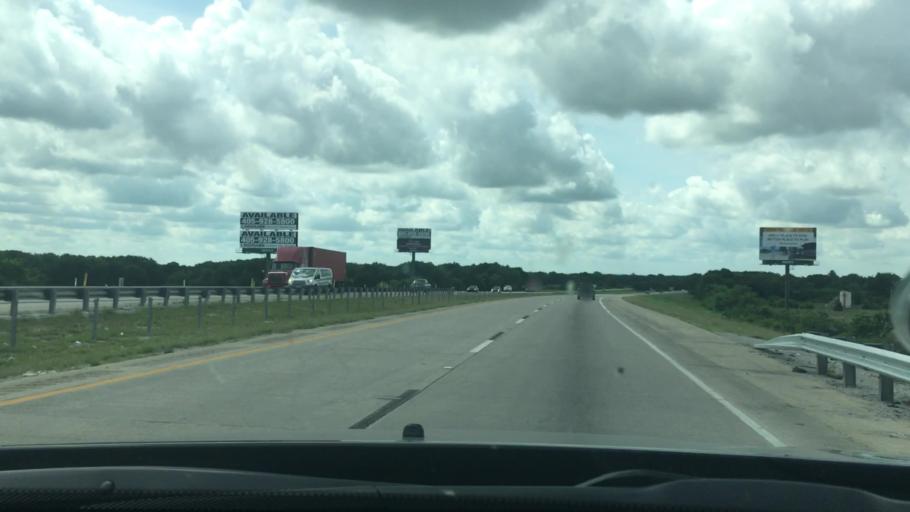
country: US
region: Oklahoma
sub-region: Love County
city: Marietta
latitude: 33.8346
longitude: -97.1317
